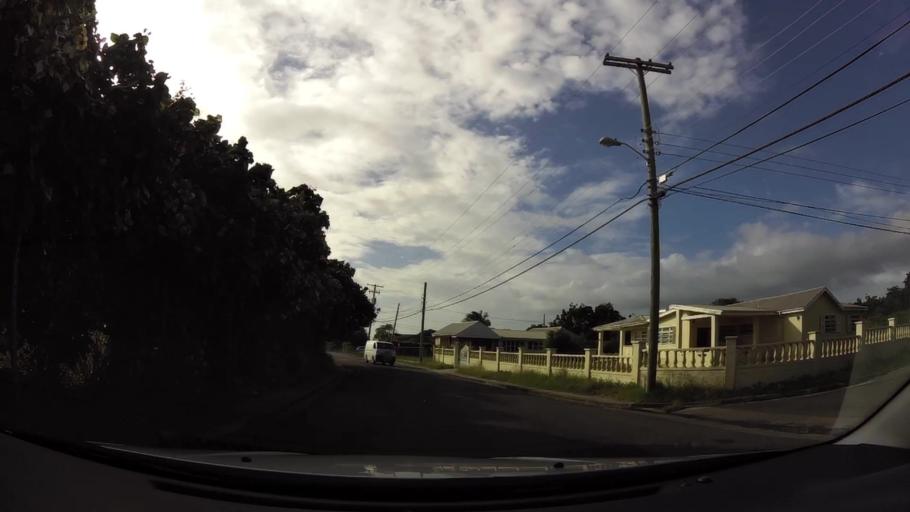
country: AG
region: Saint John
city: Saint John's
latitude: 17.1258
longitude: -61.8344
